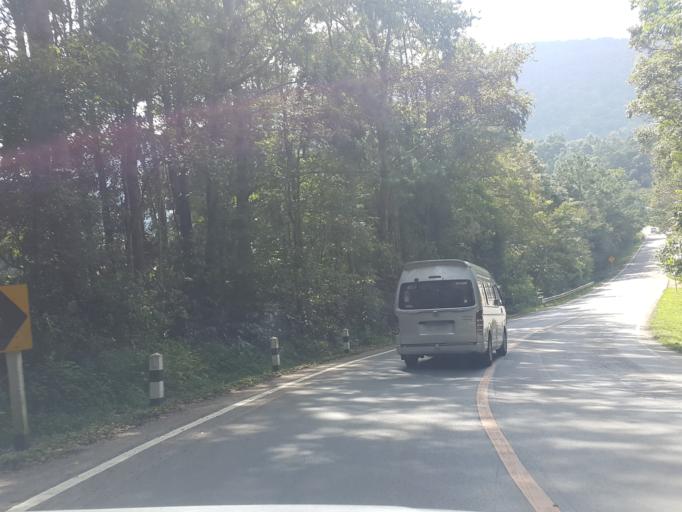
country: TH
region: Chiang Mai
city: Mae Chaem
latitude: 18.5392
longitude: 98.5276
